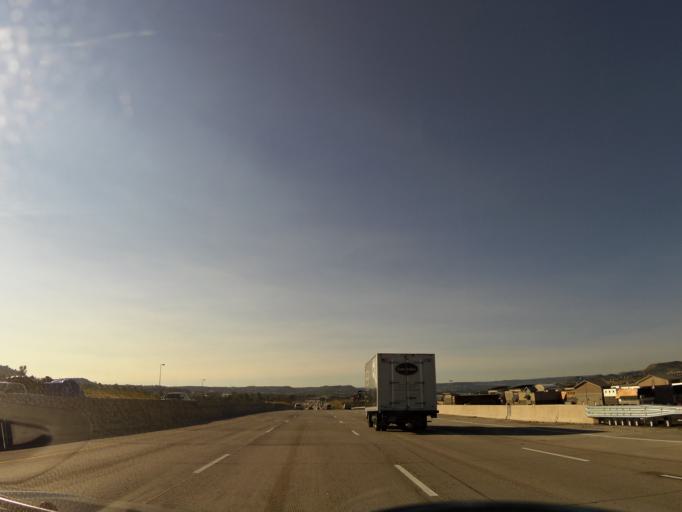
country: US
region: Colorado
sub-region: Douglas County
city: Castle Pines
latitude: 39.4248
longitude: -104.8764
